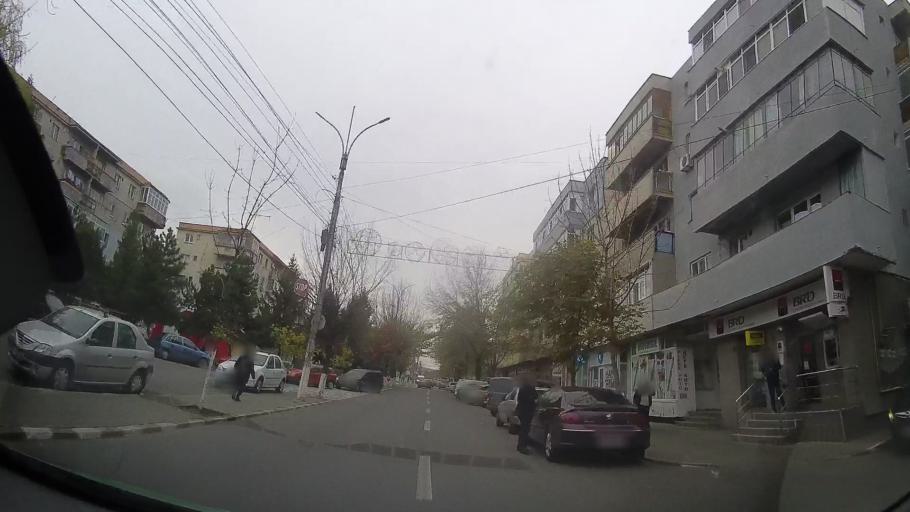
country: RO
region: Prahova
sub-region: Oras Urlati
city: Urlati
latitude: 44.9910
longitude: 26.2340
